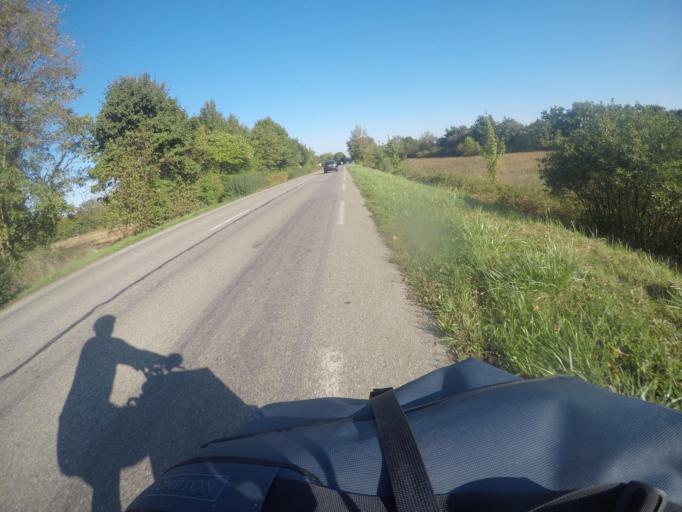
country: FR
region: Alsace
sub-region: Departement du Haut-Rhin
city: Rosenau
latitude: 47.6282
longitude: 7.5256
